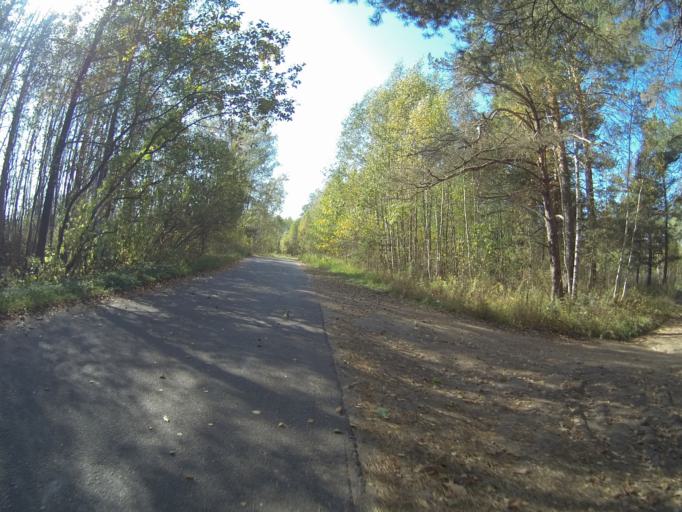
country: RU
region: Vladimir
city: Raduzhnyy
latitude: 56.0344
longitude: 40.3616
